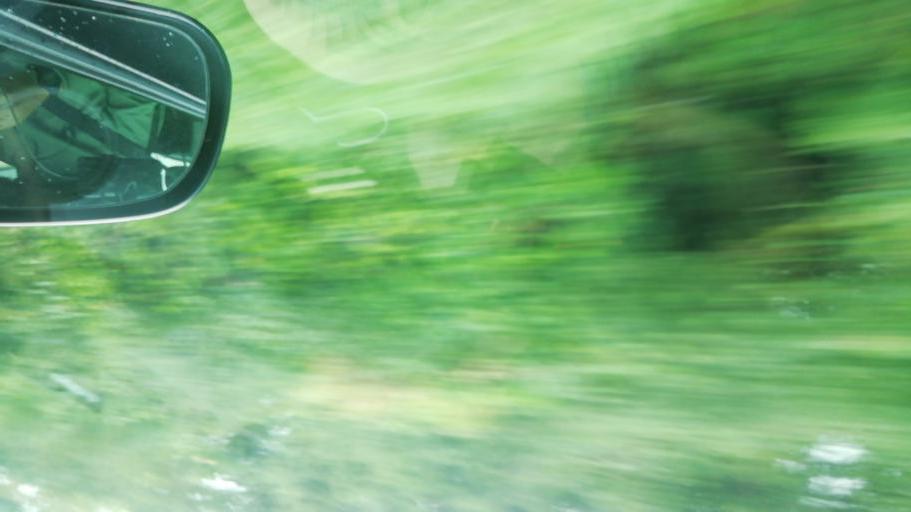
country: IE
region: Leinster
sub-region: Kilkenny
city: Thomastown
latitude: 52.5969
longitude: -7.1588
